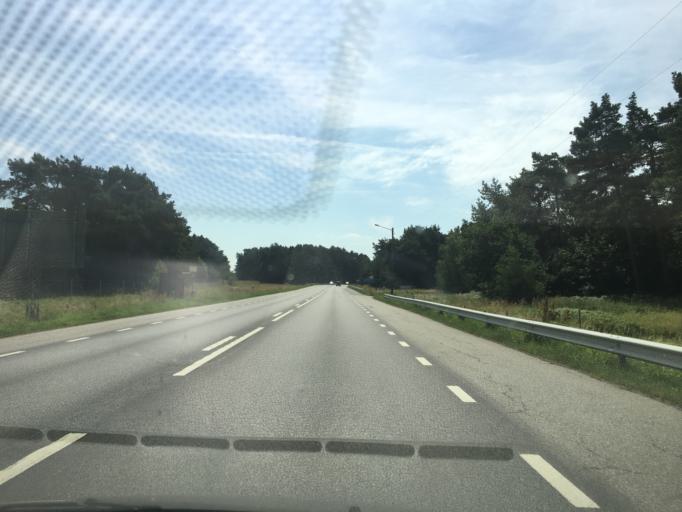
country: SE
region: Skane
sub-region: Kavlinge Kommun
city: Hofterup
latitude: 55.8365
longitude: 12.9607
